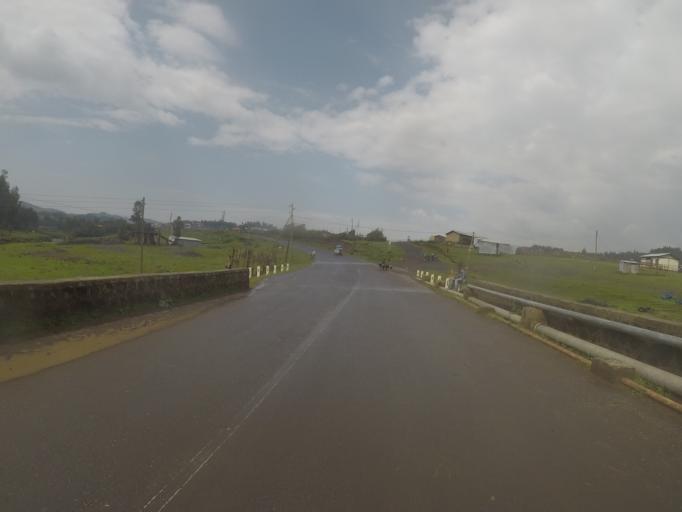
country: ET
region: Amhara
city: Debark'
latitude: 13.1298
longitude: 37.8911
